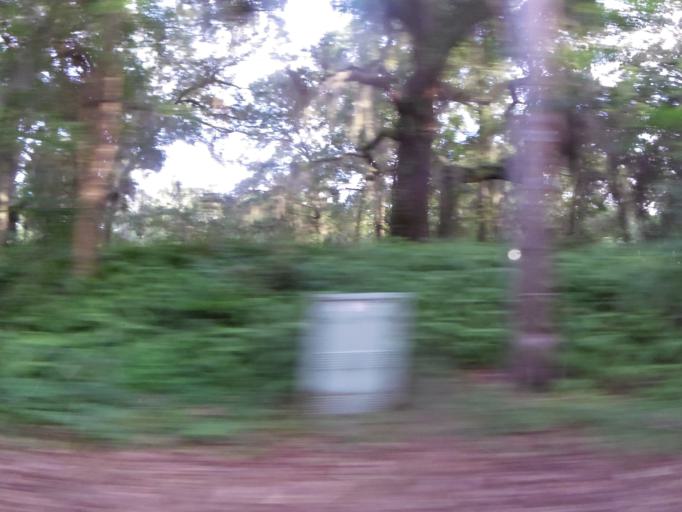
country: US
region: Florida
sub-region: Duval County
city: Jacksonville
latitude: 30.4165
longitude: -81.7120
